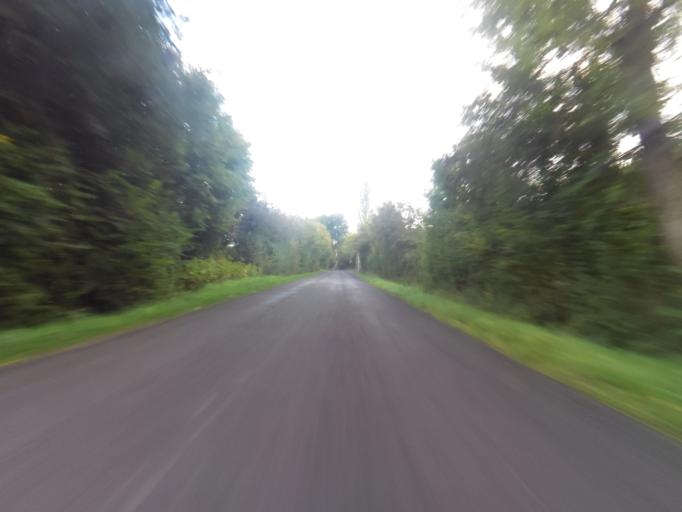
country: FR
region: Lower Normandy
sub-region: Departement de l'Orne
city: Vimoutiers
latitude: 48.9530
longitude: 0.2645
